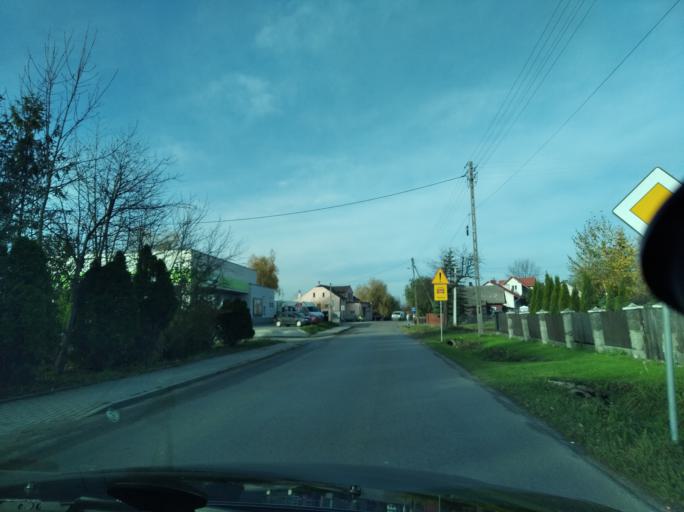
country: PL
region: Subcarpathian Voivodeship
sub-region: Powiat rzeszowski
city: Krasne
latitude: 50.0322
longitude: 22.0972
